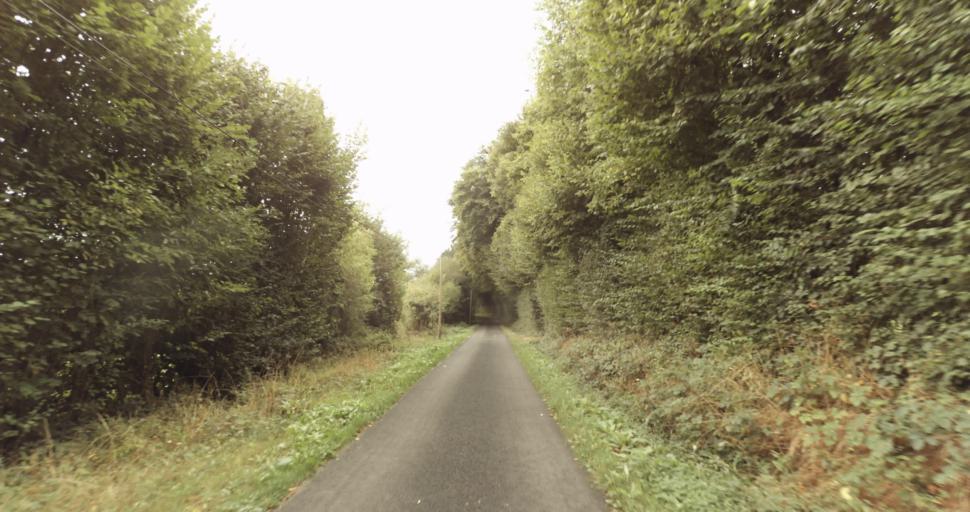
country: FR
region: Lower Normandy
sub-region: Departement de l'Orne
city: Gace
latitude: 48.8511
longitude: 0.2838
